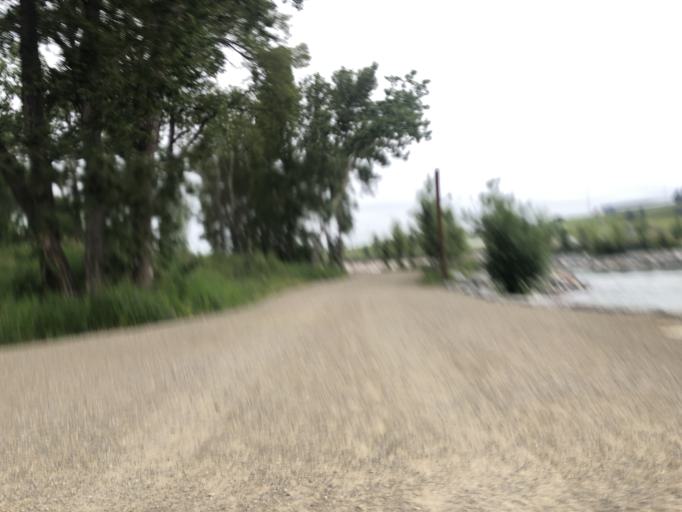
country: CA
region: Alberta
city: Calgary
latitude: 51.0422
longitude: -114.0133
